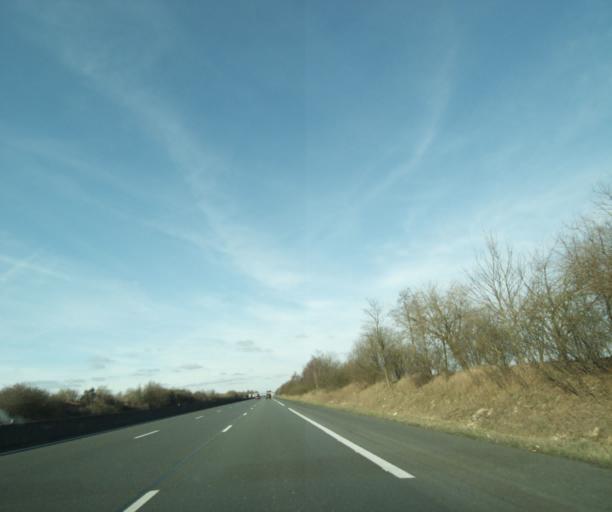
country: FR
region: Centre
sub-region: Departement d'Eure-et-Loir
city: Aunay-sous-Auneau
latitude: 48.4228
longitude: 1.9005
